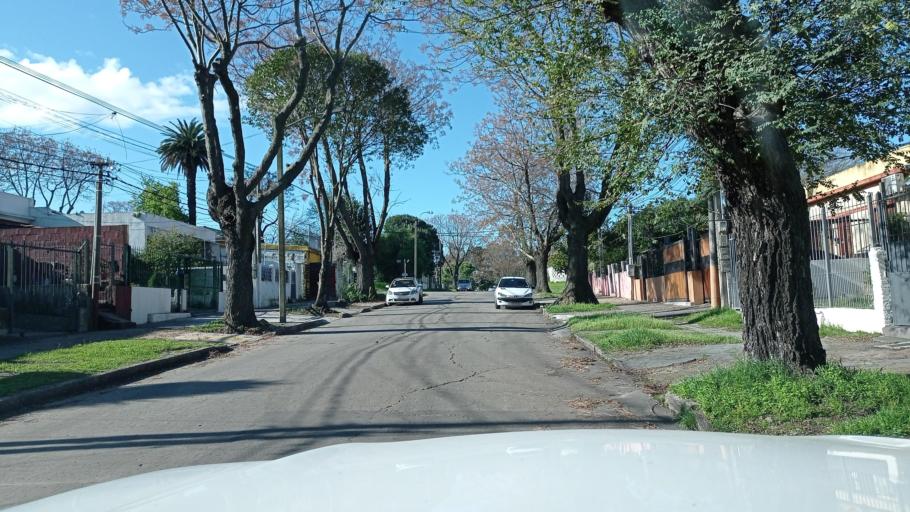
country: UY
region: Montevideo
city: Montevideo
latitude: -34.8469
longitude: -56.2190
